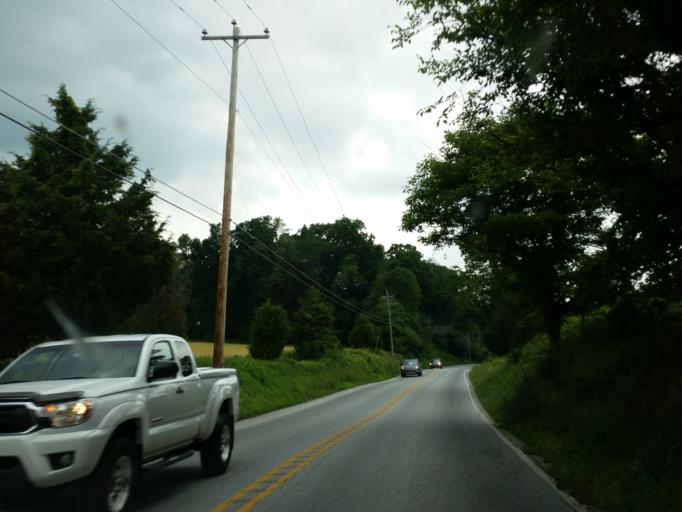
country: US
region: Pennsylvania
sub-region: Chester County
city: Oxford
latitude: 39.8563
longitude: -75.9728
